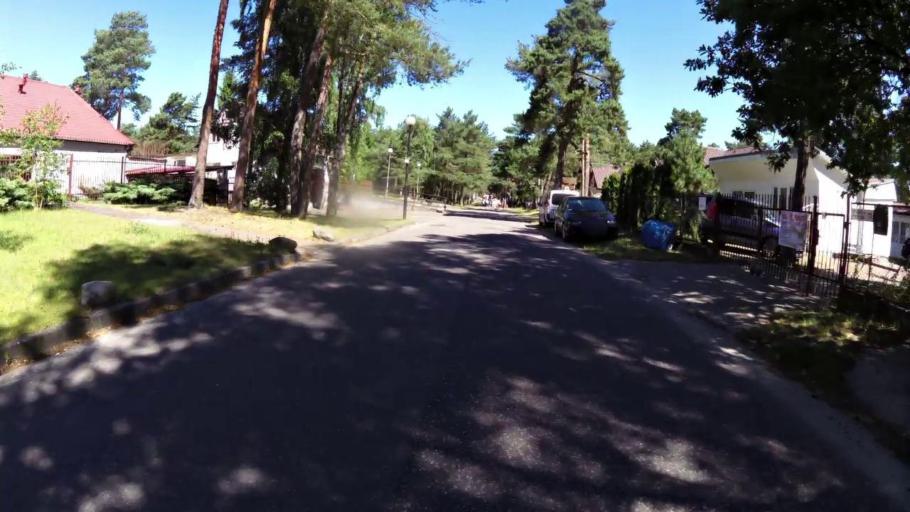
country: PL
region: West Pomeranian Voivodeship
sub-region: Powiat gryficki
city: Pobierowo
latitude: 54.0540
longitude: 14.9193
